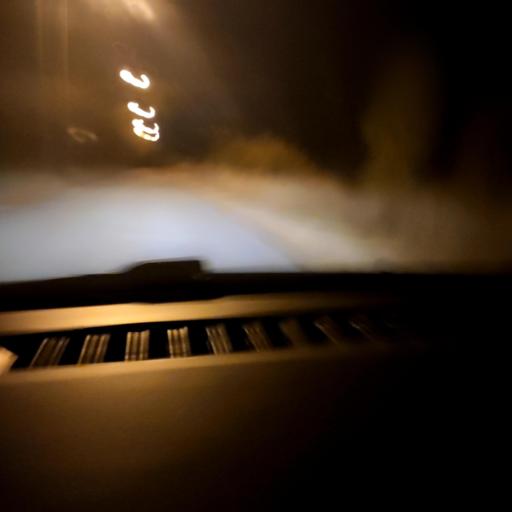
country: RU
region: Voronezj
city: Pridonskoy
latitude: 51.6847
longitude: 39.0926
